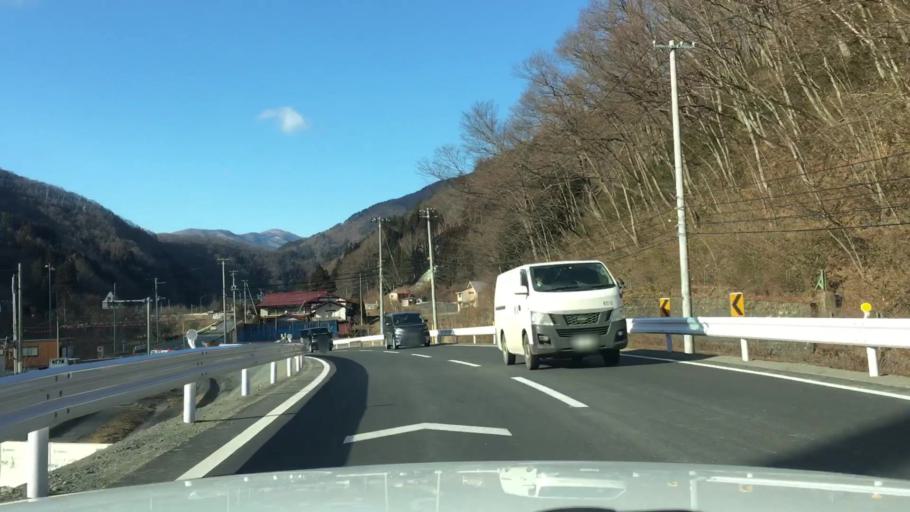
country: JP
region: Iwate
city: Tono
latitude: 39.6116
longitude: 141.6310
